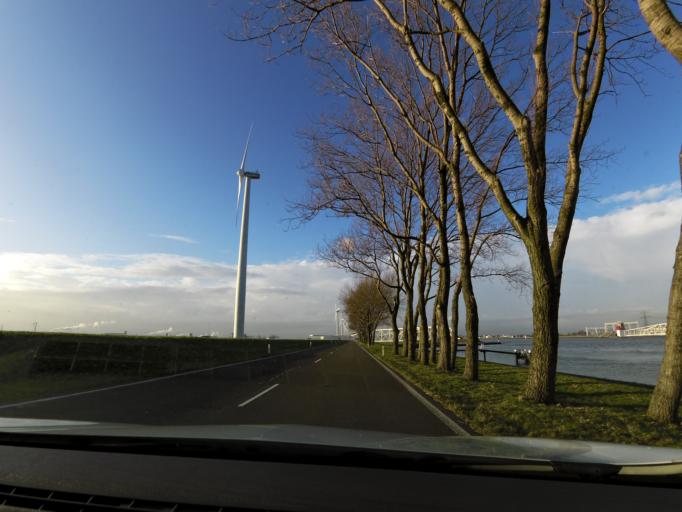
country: NL
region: South Holland
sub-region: Gemeente Rotterdam
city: Hoek van Holland
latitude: 51.9492
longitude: 4.1668
